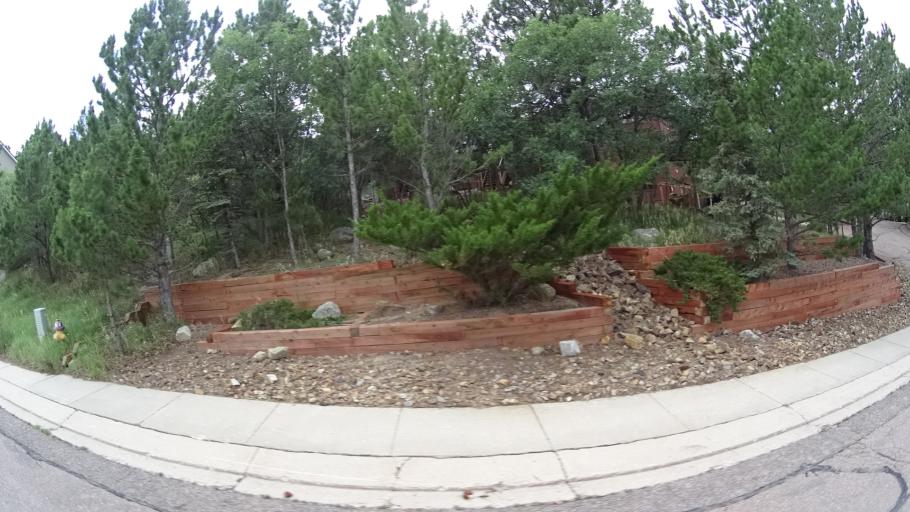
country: US
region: Colorado
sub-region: El Paso County
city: Colorado Springs
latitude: 38.9078
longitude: -104.8440
